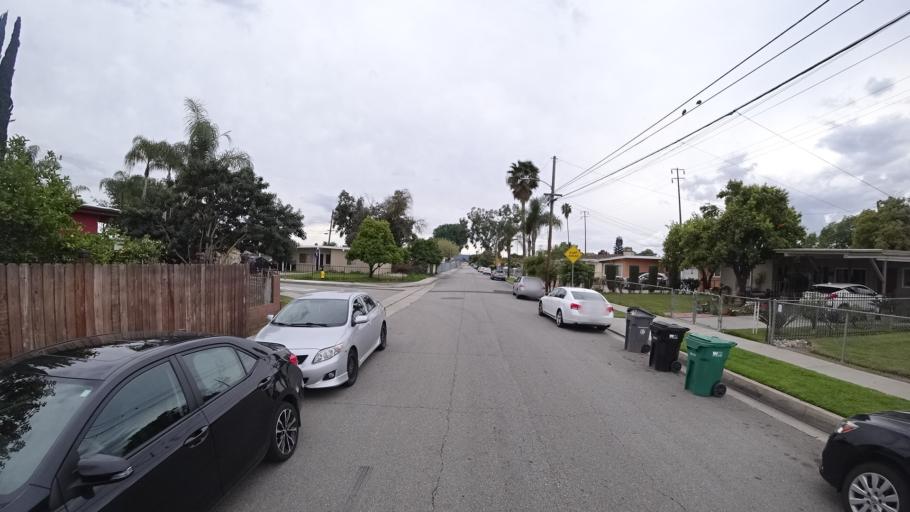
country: US
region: California
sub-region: Los Angeles County
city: Baldwin Park
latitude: 34.0857
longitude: -117.9509
